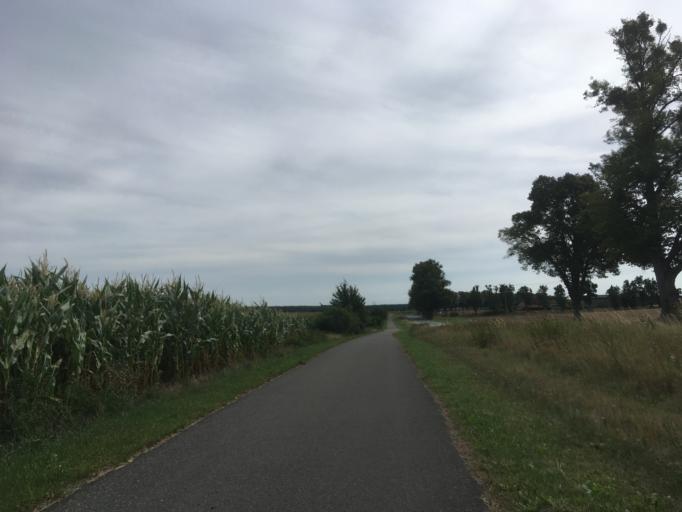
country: DE
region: Brandenburg
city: Mittenwalde
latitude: 53.2552
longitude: 13.6288
